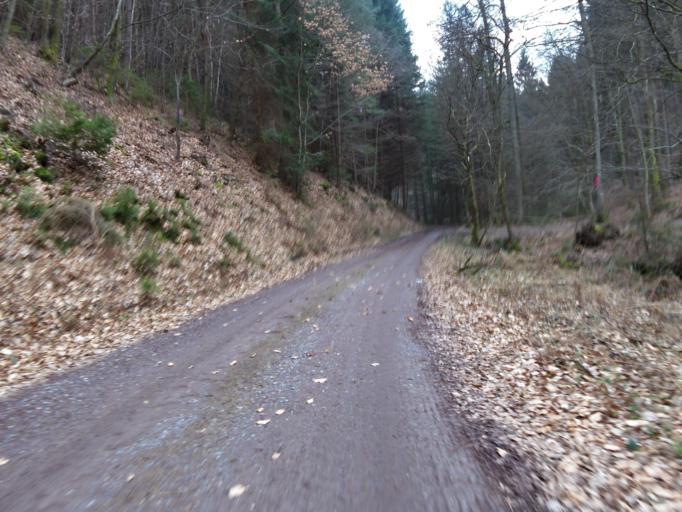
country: DE
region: Rheinland-Pfalz
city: Carlsberg
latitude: 49.4620
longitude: 8.0227
